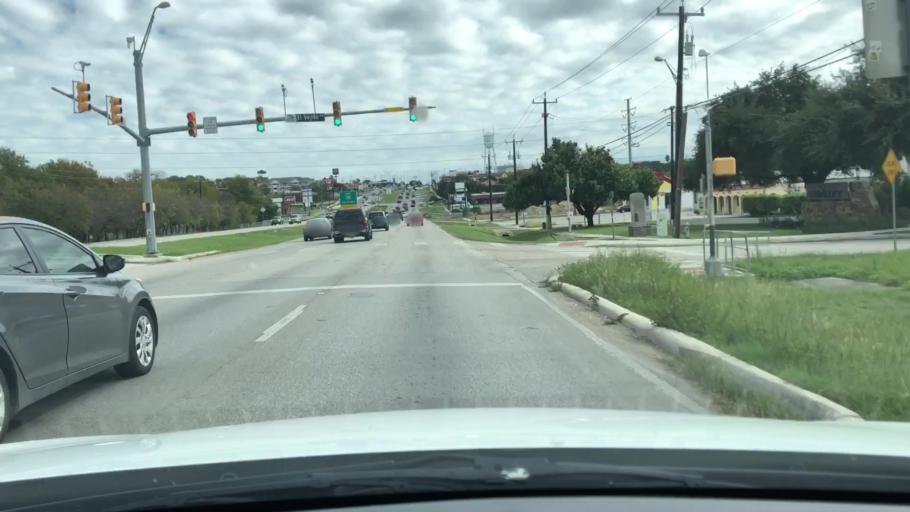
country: US
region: Texas
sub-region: Bexar County
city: Leon Valley
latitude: 29.4933
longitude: -98.6164
